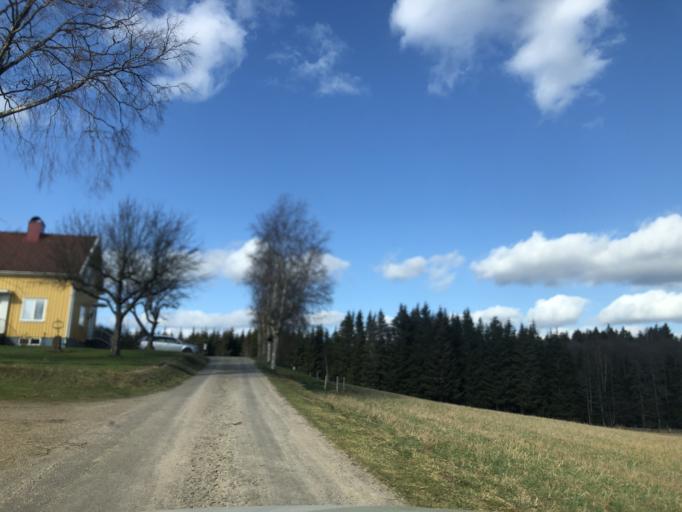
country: SE
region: Vaestra Goetaland
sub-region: Ulricehamns Kommun
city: Ulricehamn
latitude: 57.6853
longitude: 13.3776
